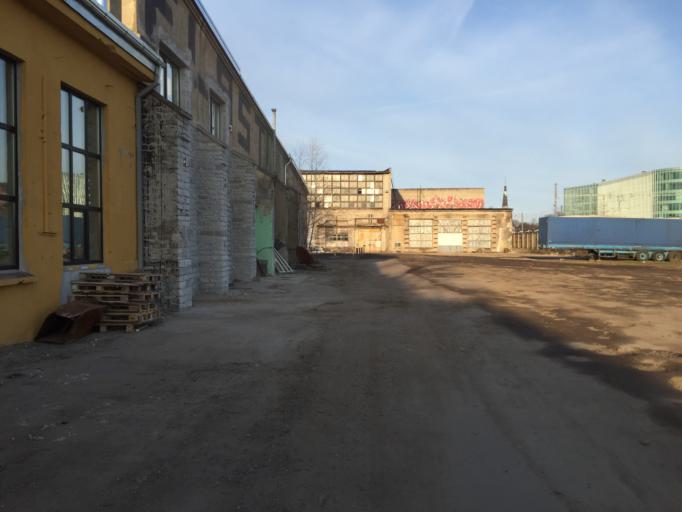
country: EE
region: Harju
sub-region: Tallinna linn
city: Tallinn
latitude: 59.4381
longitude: 24.7294
